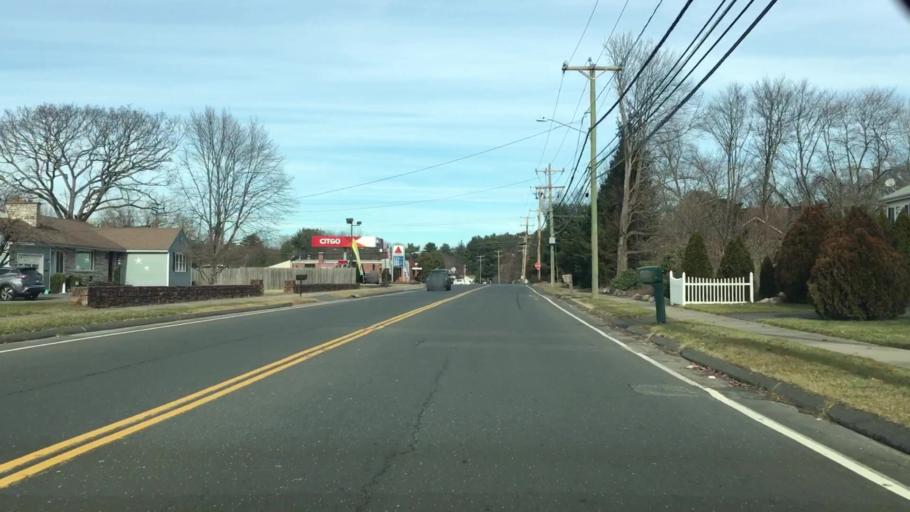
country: US
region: Connecticut
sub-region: Hartford County
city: Plainville
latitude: 41.6564
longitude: -72.9013
